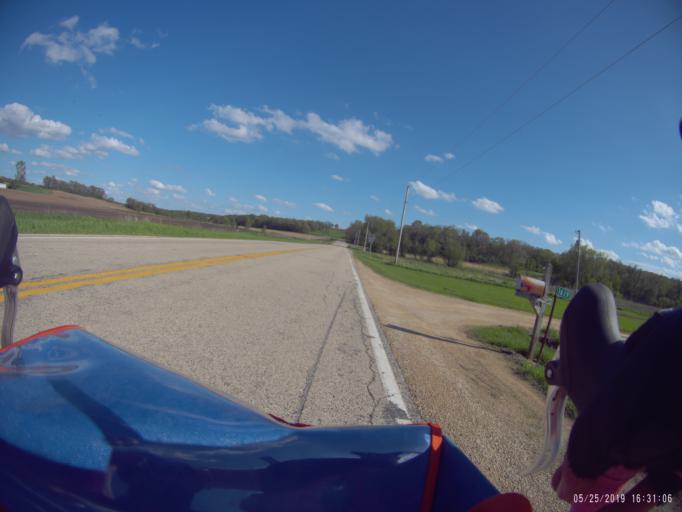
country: US
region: Wisconsin
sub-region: Dane County
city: Mount Horeb
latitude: 42.9445
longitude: -89.7196
